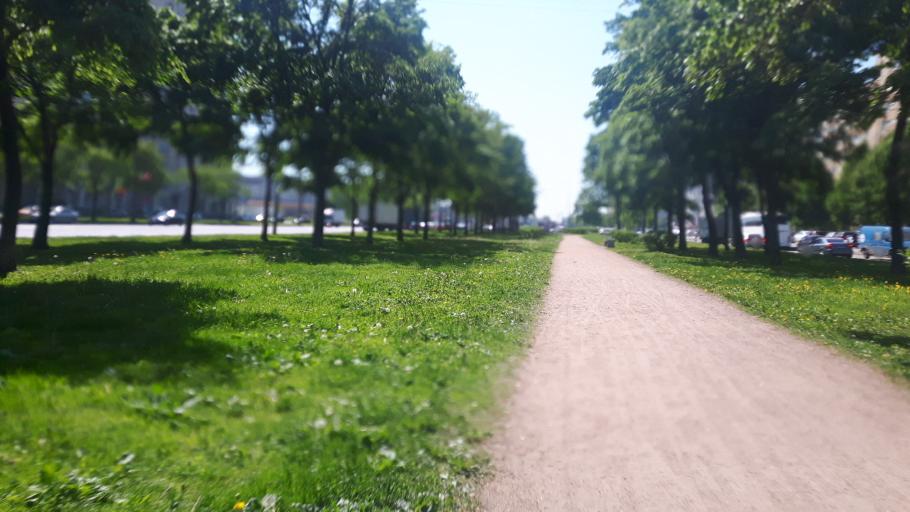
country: RU
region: St.-Petersburg
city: Dachnoye
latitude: 59.8548
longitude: 30.2251
